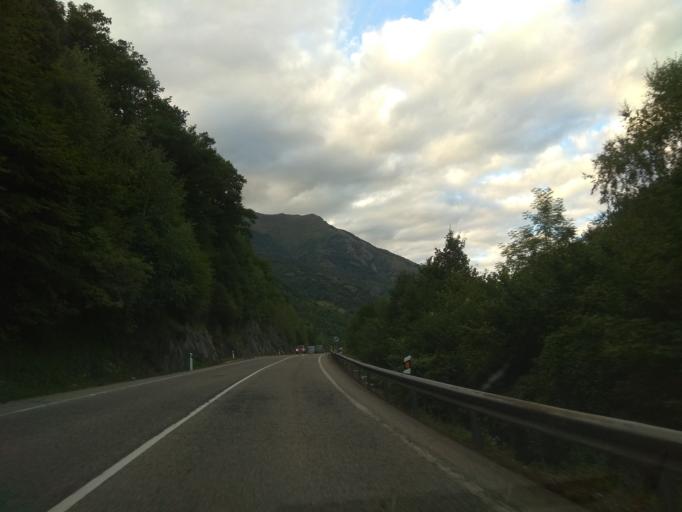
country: ES
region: Catalonia
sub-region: Provincia de Lleida
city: Les
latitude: 42.7662
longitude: 0.6867
